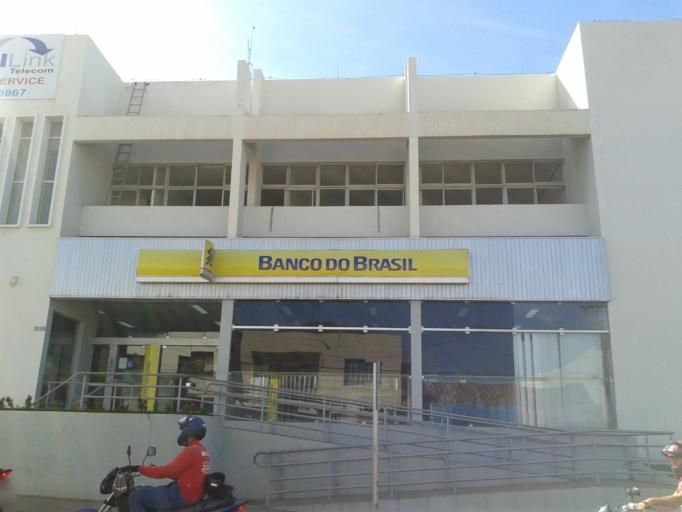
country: BR
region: Bahia
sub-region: Livramento Do Brumado
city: Livramento do Brumado
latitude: -13.6505
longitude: -41.8426
